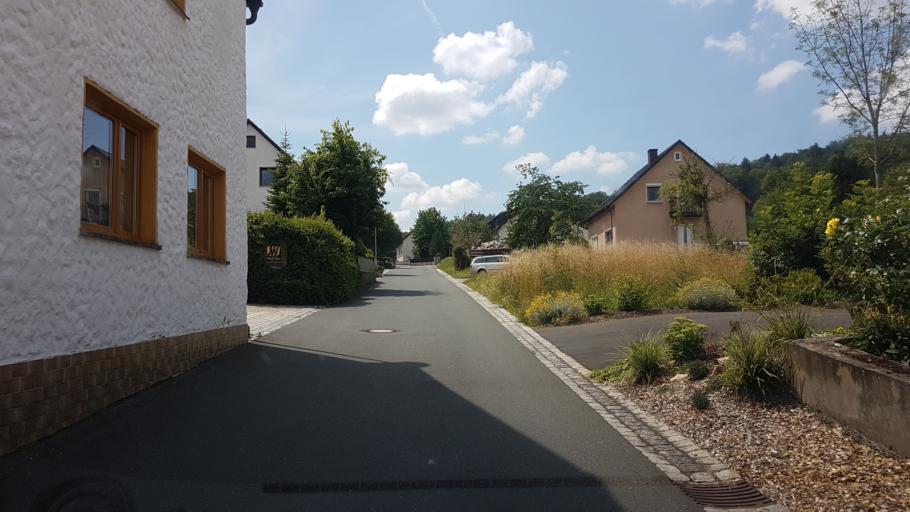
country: DE
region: Bavaria
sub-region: Upper Franconia
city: Gossweinstein
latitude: 49.7788
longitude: 11.2882
